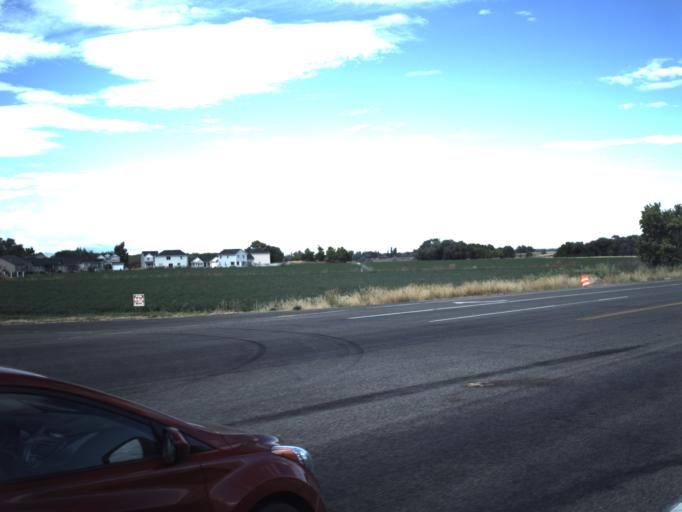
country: US
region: Utah
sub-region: Cache County
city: Wellsville
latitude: 41.6492
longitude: -111.9098
